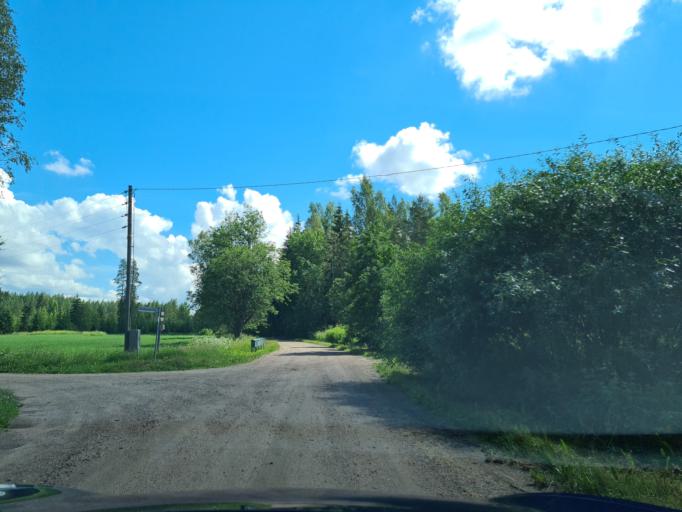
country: FI
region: Uusimaa
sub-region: Helsinki
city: Kaerkoelae
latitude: 60.7551
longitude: 23.9532
